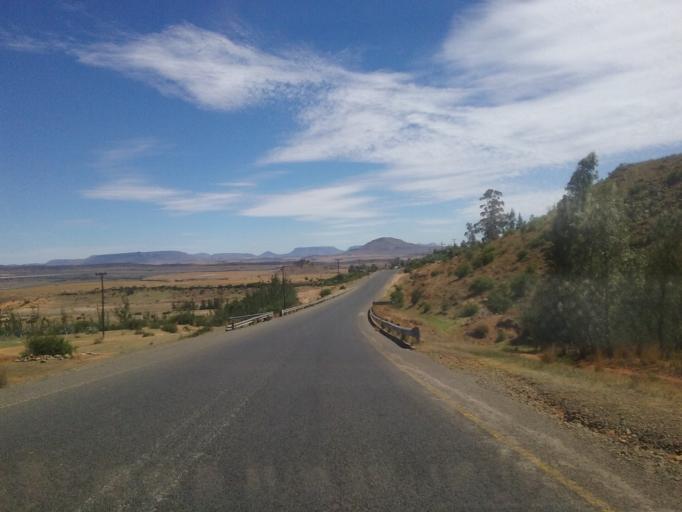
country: LS
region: Mohale's Hoek District
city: Mohale's Hoek
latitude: -30.1983
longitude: 27.4160
